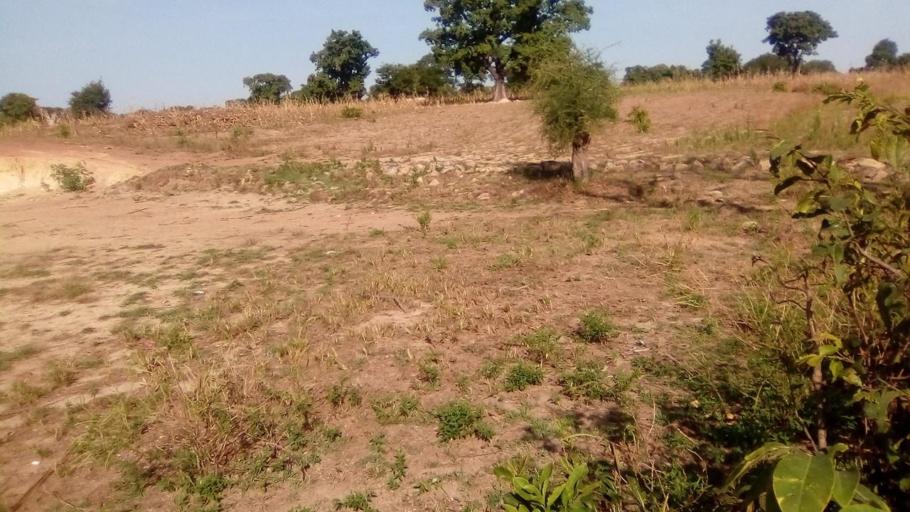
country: TG
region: Savanes
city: Dapaong
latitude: 11.0571
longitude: 0.1245
